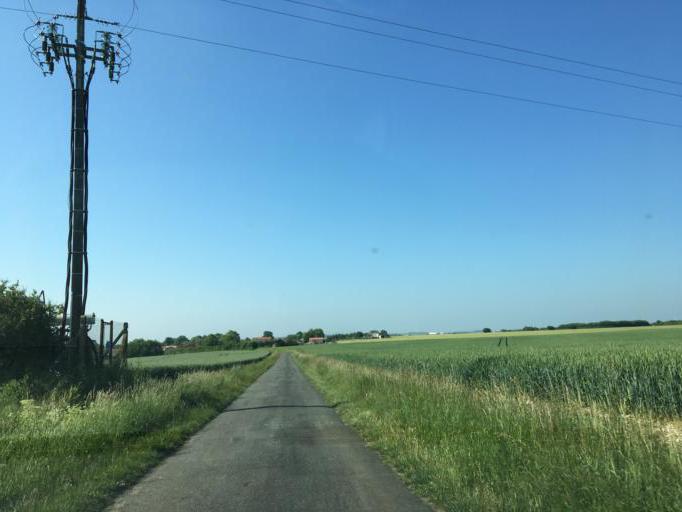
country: FR
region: Poitou-Charentes
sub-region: Departement des Deux-Sevres
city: Beauvoir-sur-Niort
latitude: 46.0807
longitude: -0.5080
